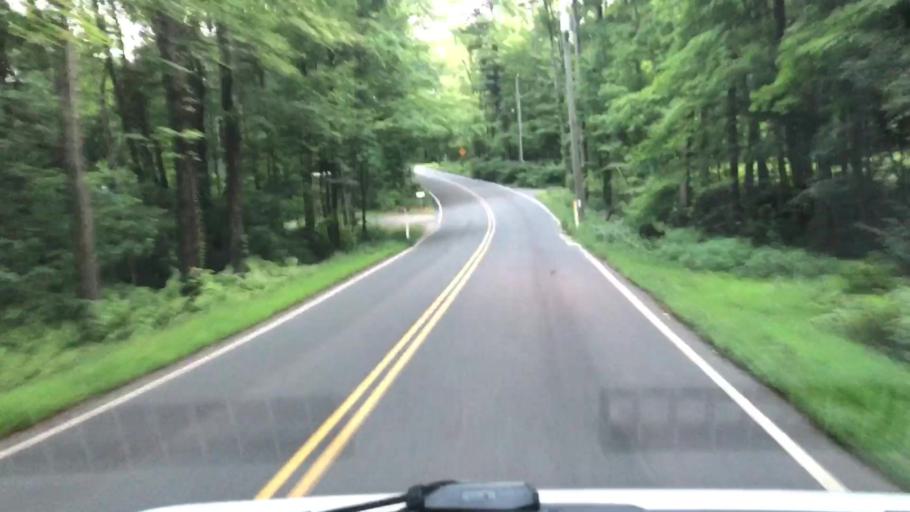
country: US
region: Massachusetts
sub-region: Hampshire County
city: Southampton
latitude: 42.2563
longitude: -72.7324
